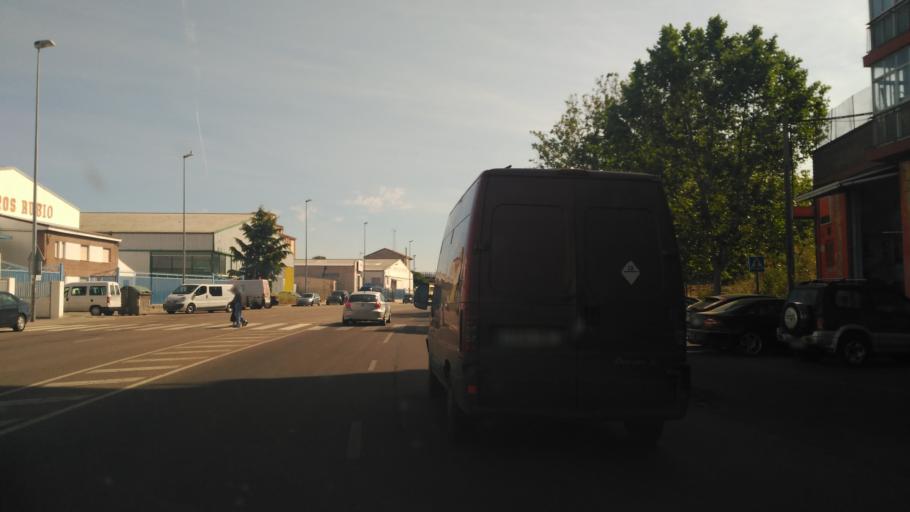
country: ES
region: Castille and Leon
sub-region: Provincia de Zamora
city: Zamora
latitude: 41.5115
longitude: -5.7467
